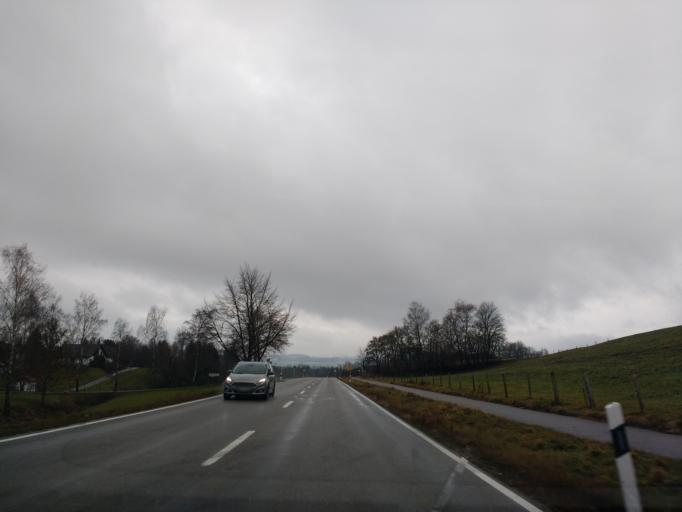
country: DE
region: Bavaria
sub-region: Swabia
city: Neuburg
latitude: 47.7745
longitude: 10.3475
